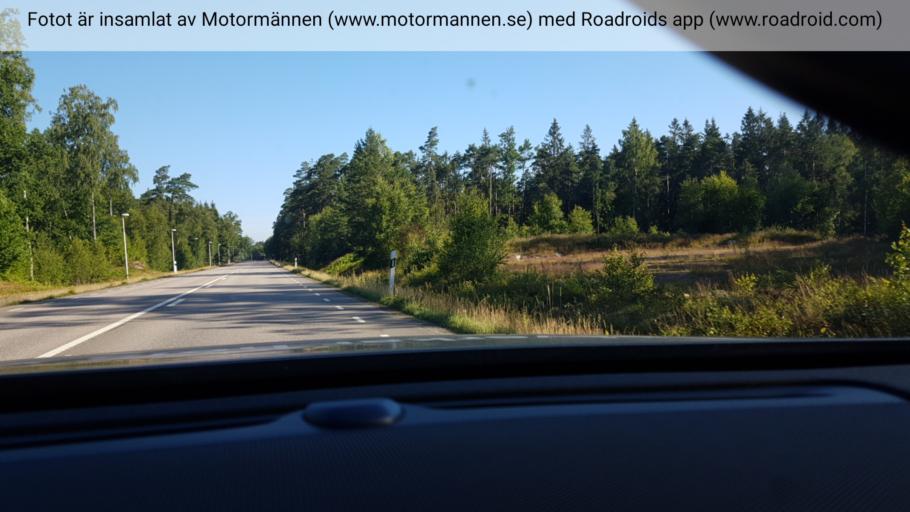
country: SE
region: Skane
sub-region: Hassleholms Kommun
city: Bjarnum
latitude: 56.3199
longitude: 13.6848
